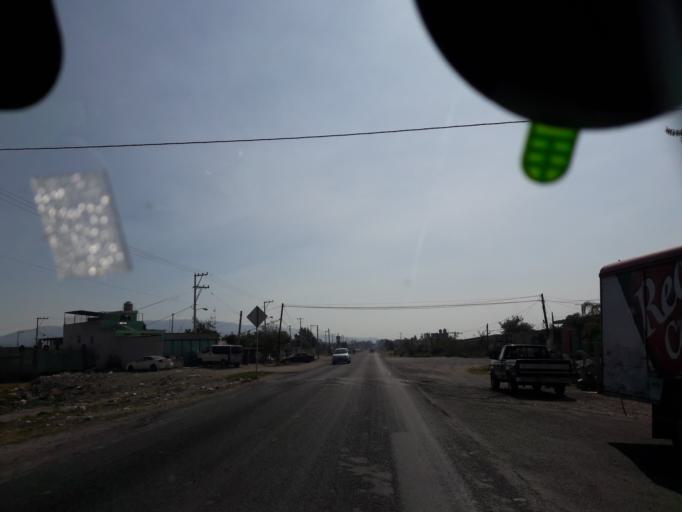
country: MX
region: Tlaxcala
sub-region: Ixtacuixtla de Mariano Matamoros
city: Santa Justina Ecatepec
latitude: 19.3122
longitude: -98.3417
